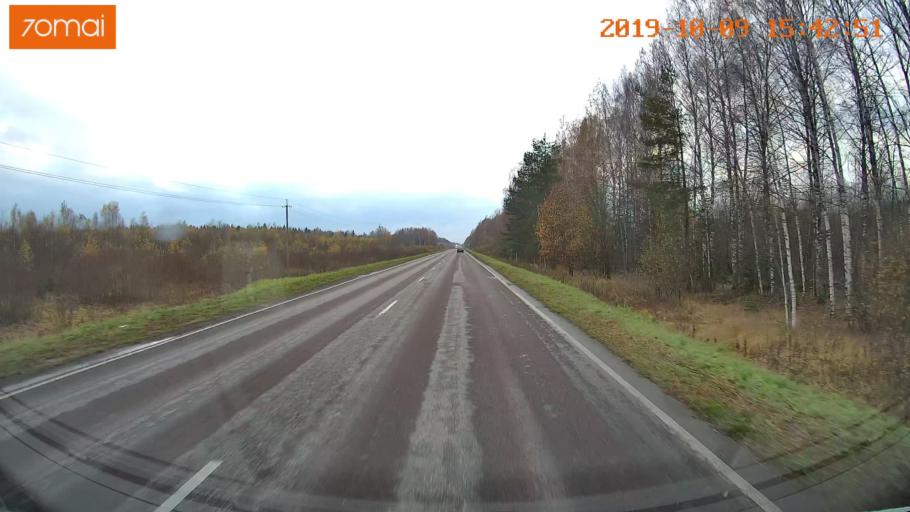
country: RU
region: Kostroma
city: Oktyabr'skiy
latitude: 57.8640
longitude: 41.0993
